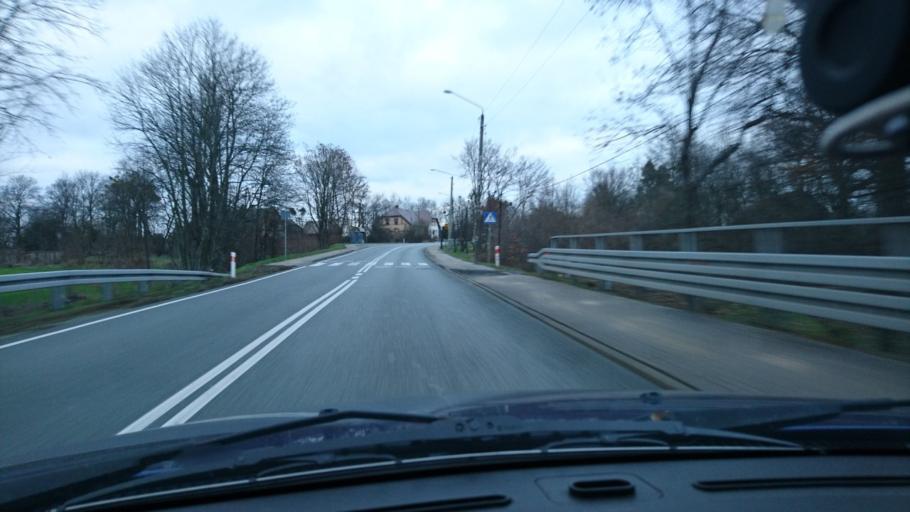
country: PL
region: Opole Voivodeship
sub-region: Powiat kluczborski
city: Byczyna
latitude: 51.0627
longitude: 18.2009
